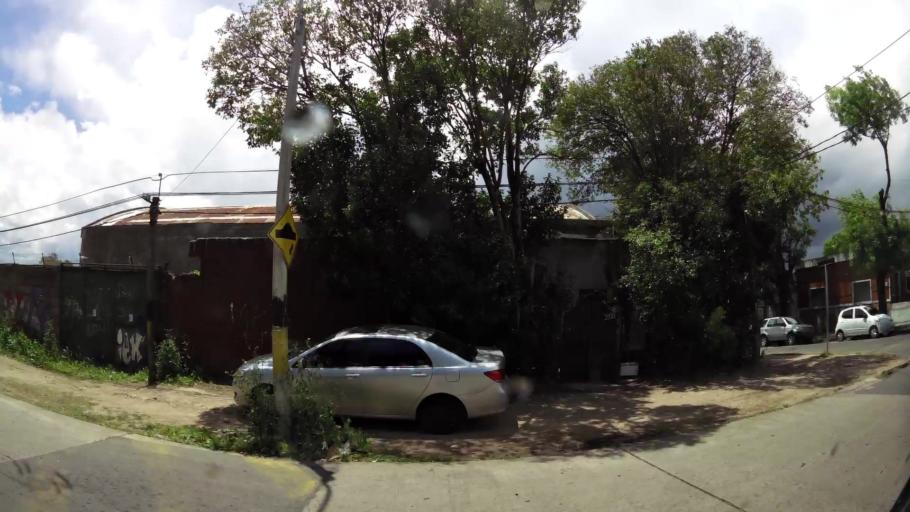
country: UY
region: Montevideo
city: Montevideo
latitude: -34.8673
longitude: -56.1679
